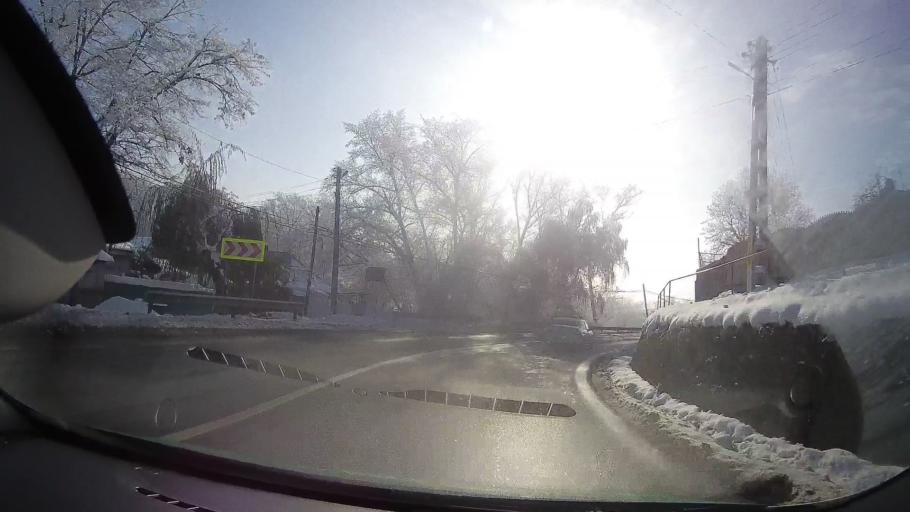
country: RO
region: Iasi
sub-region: Comuna Motca
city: Motca
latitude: 47.2361
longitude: 26.6037
